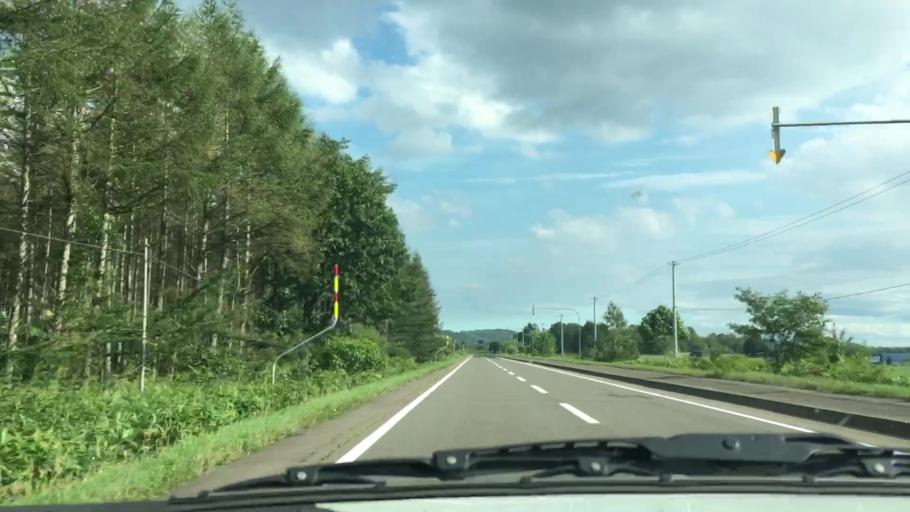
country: JP
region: Hokkaido
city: Otofuke
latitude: 43.3278
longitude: 143.2965
